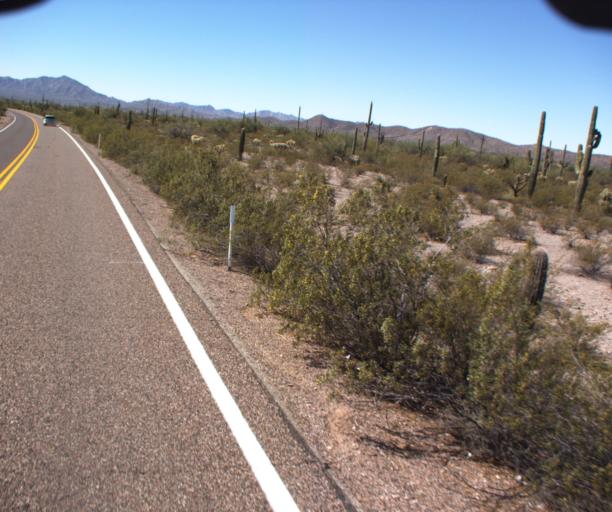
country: MX
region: Sonora
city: Sonoyta
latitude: 31.9100
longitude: -112.8100
